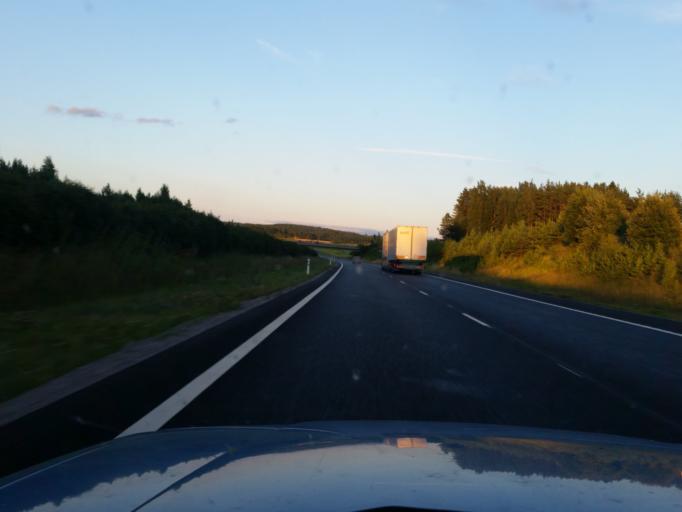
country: FI
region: Varsinais-Suomi
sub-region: Salo
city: Pertteli
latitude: 60.3916
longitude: 23.2722
